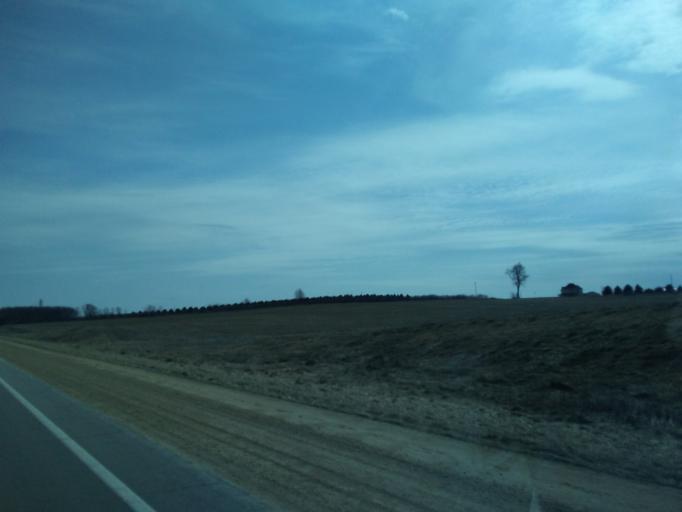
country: US
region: Iowa
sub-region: Winneshiek County
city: Decorah
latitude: 43.3745
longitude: -91.8138
